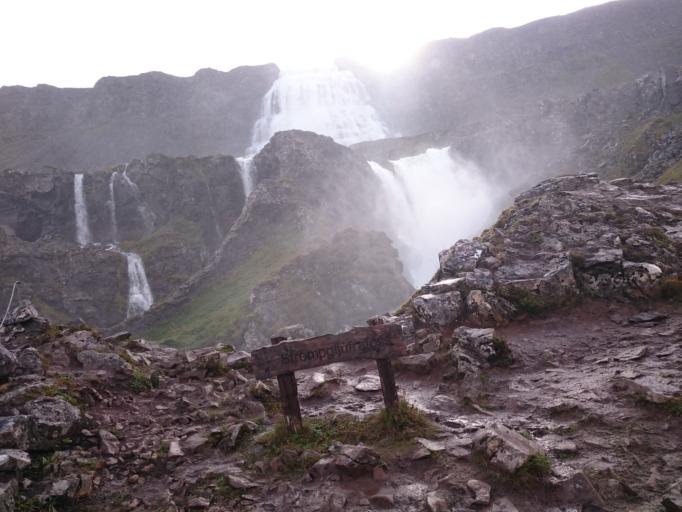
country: IS
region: Westfjords
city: Isafjoerdur
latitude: 65.7345
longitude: -23.2044
